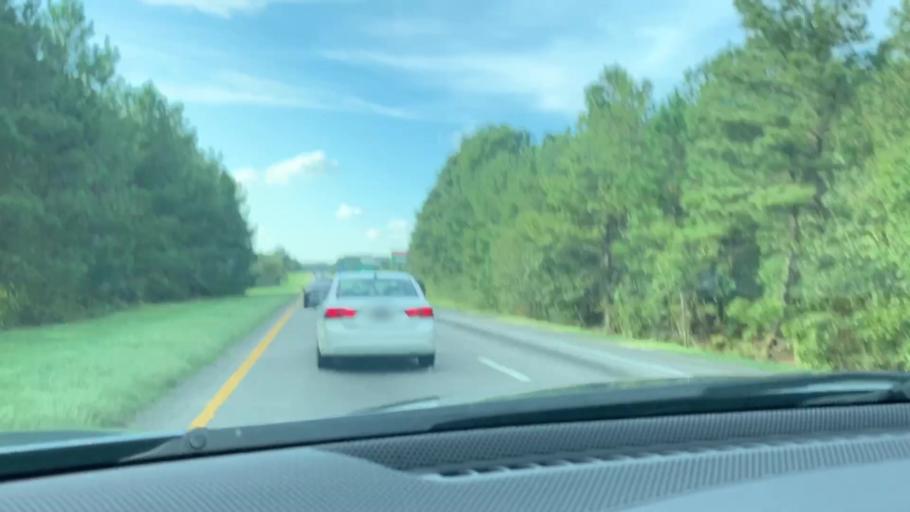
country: US
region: South Carolina
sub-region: Orangeburg County
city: Brookdale
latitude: 33.4449
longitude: -80.7128
